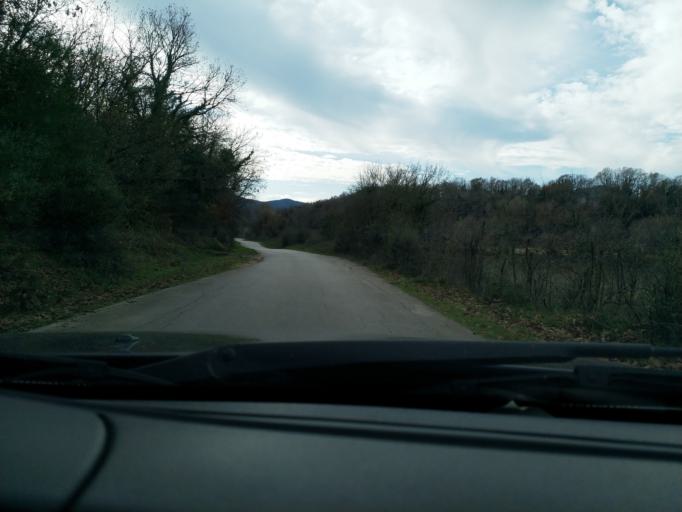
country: GR
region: Epirus
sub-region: Nomos Prevezis
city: Filippiada
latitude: 39.2322
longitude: 20.8446
